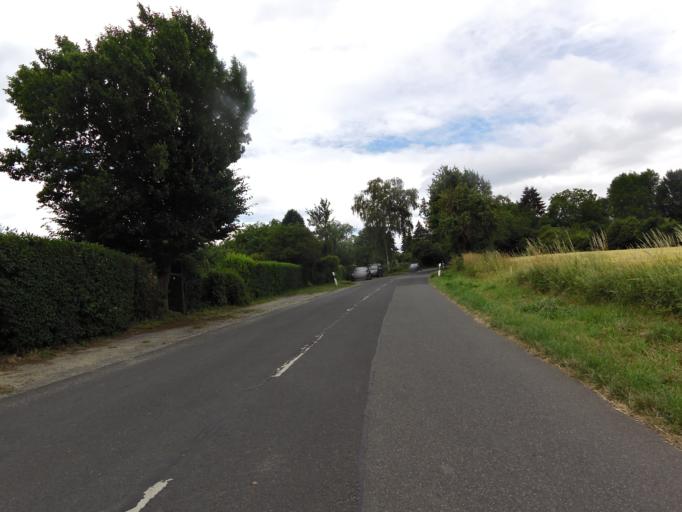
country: DE
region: Bavaria
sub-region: Regierungsbezirk Unterfranken
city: Reichenberg
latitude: 49.7554
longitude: 9.9338
